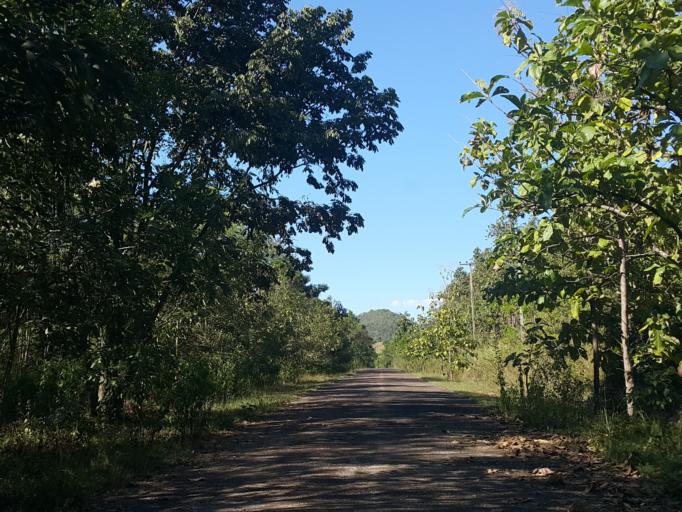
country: TH
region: Chiang Mai
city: San Sai
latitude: 18.9197
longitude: 99.1159
